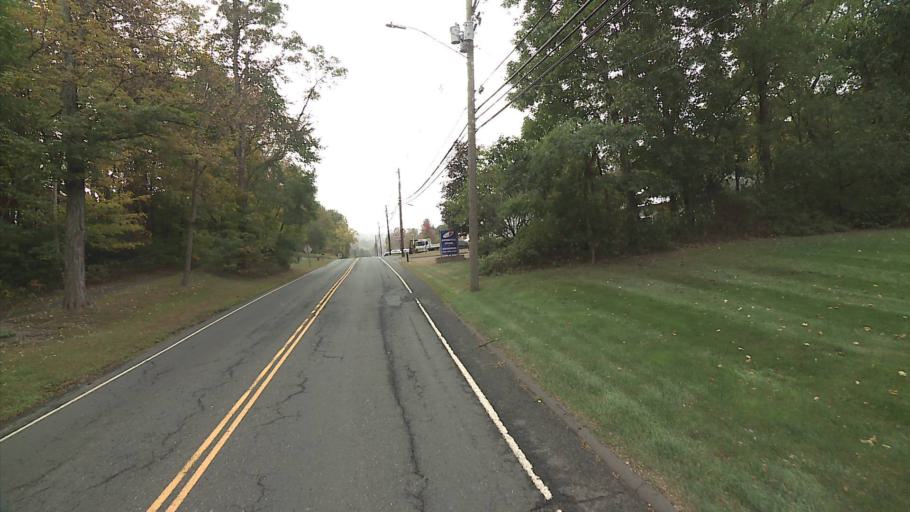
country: US
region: Connecticut
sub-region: Litchfield County
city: Woodbury Center
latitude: 41.5314
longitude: -73.2050
